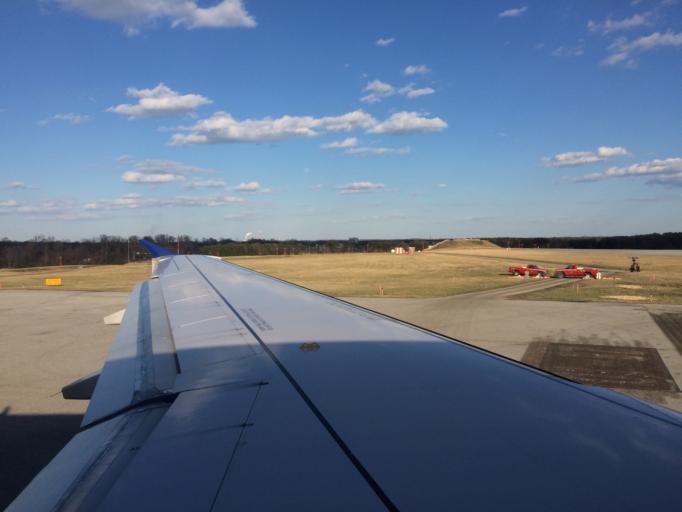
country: US
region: Maryland
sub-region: Anne Arundel County
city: Ferndale
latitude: 39.1739
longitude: -76.6552
